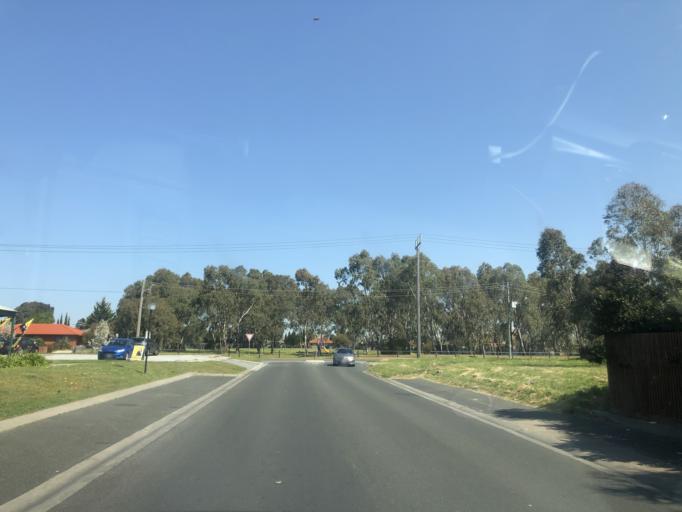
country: AU
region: Victoria
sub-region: Casey
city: Hampton Park
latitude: -38.0348
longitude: 145.2654
